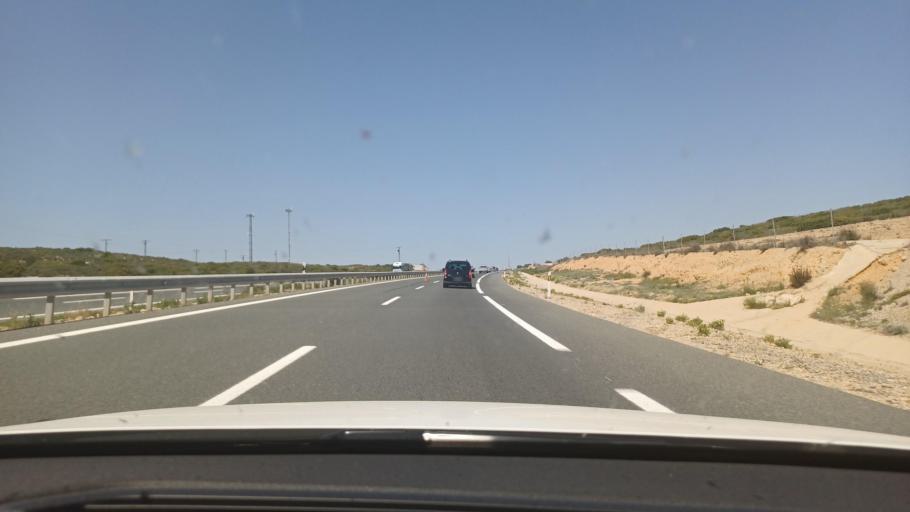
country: ES
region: Castille-La Mancha
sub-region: Provincia de Albacete
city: Alpera
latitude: 38.8785
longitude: -1.1954
